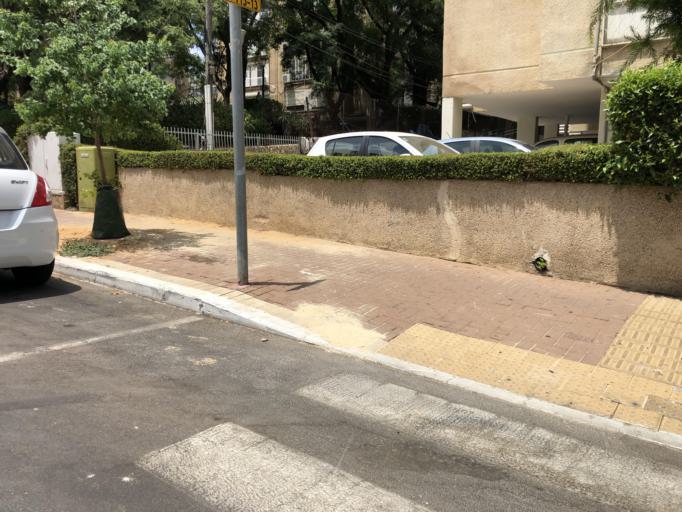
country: IL
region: Tel Aviv
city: Bene Beraq
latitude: 32.0615
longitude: 34.8299
